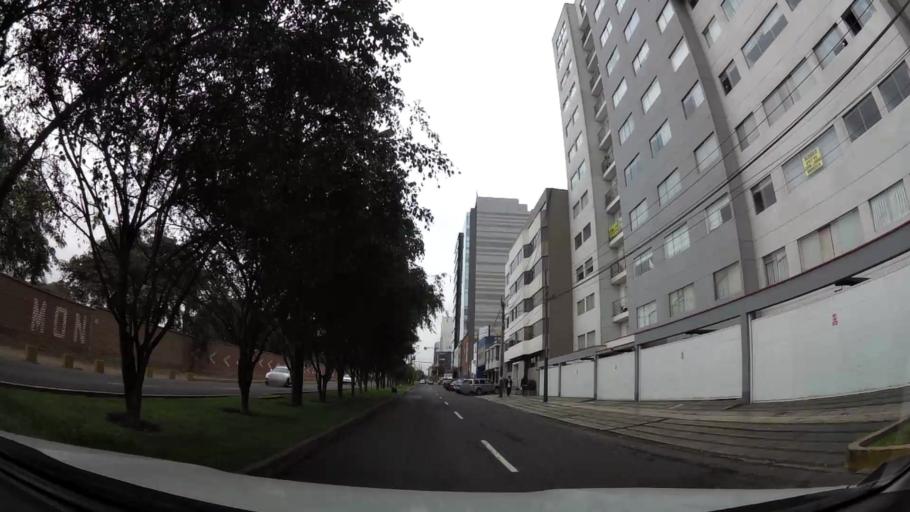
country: PE
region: Lima
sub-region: Lima
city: La Molina
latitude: -12.0924
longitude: -76.9738
